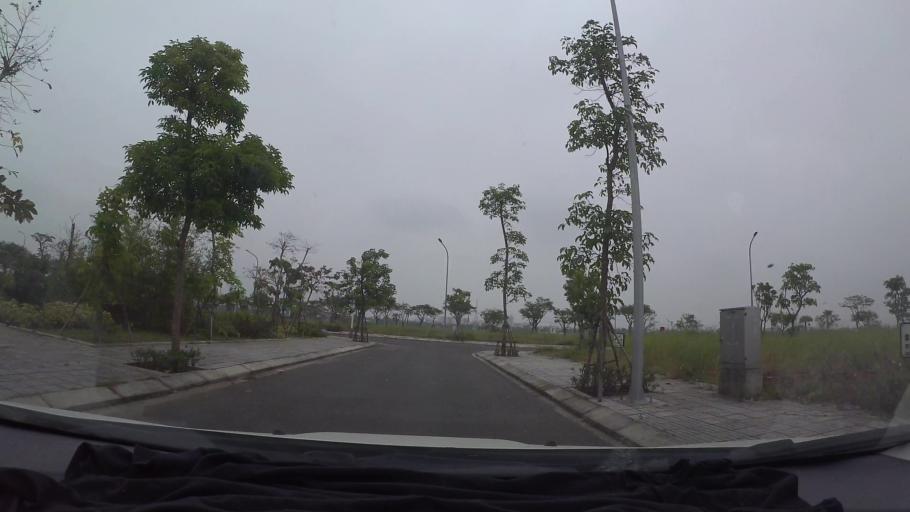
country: VN
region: Da Nang
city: Son Tra
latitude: 16.0340
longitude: 108.2330
